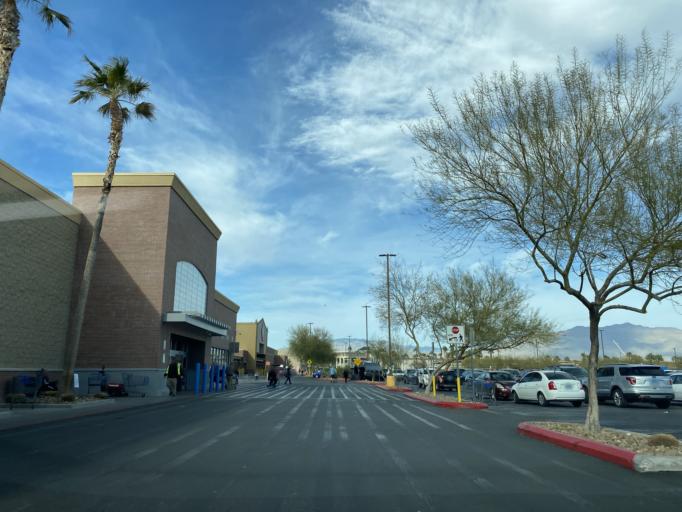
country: US
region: Nevada
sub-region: Clark County
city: Las Vegas
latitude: 36.2717
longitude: -115.2702
